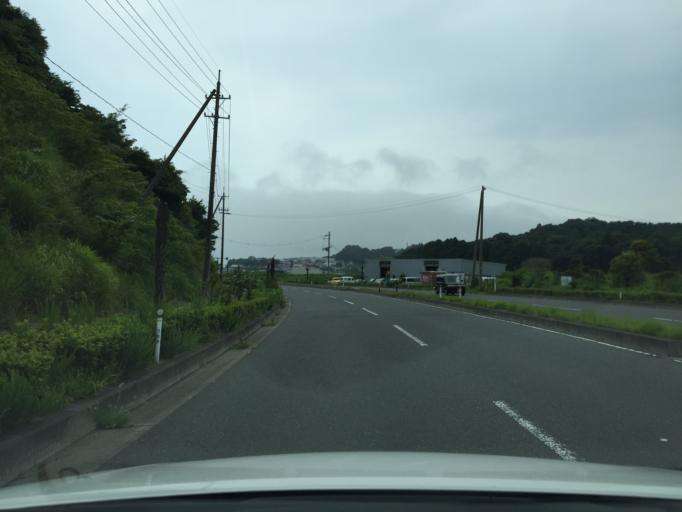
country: JP
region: Fukushima
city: Iwaki
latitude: 36.9565
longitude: 140.9189
